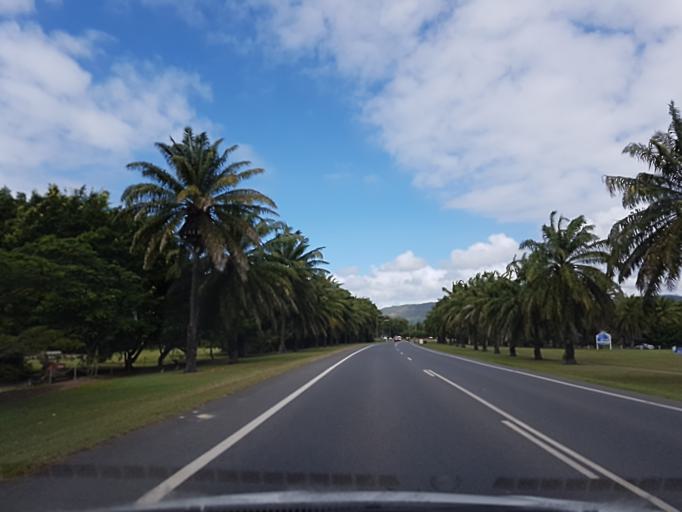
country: AU
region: Queensland
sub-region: Cairns
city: Port Douglas
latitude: -16.5033
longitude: 145.4633
